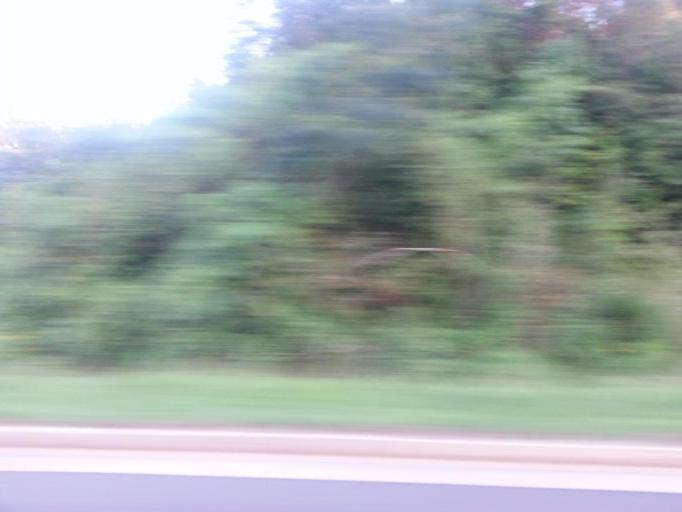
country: US
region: Tennessee
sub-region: Roane County
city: Kingston
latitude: 35.8828
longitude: -84.4270
